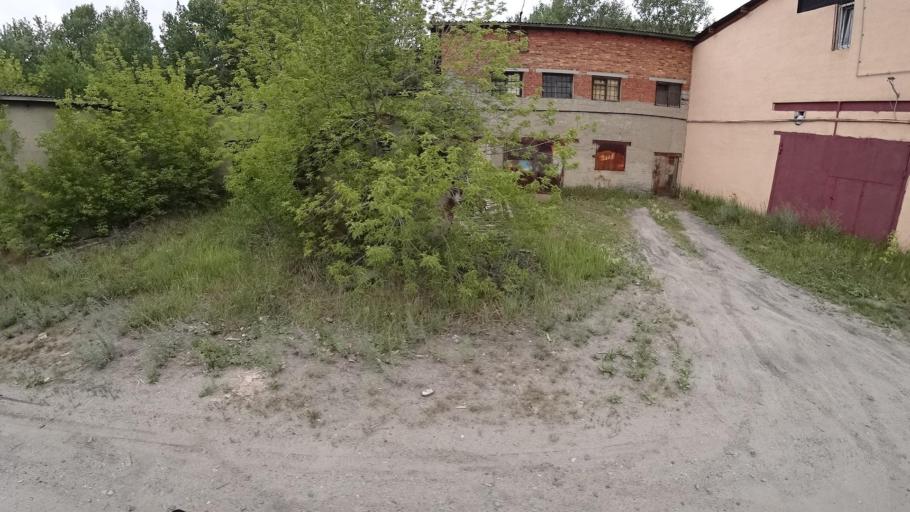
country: RU
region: Sverdlovsk
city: Kamyshlov
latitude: 56.8296
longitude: 62.7286
